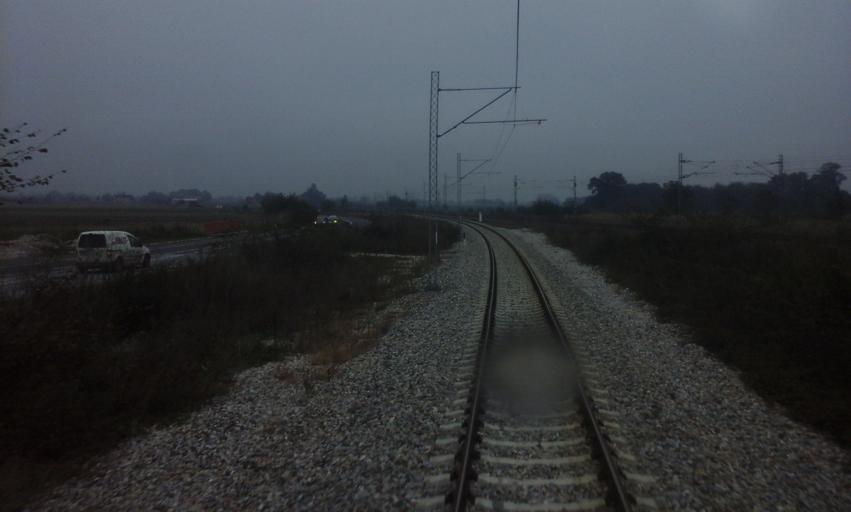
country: RS
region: Central Serbia
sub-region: Pomoravski Okrug
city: Paracin
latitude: 43.8867
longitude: 21.3833
